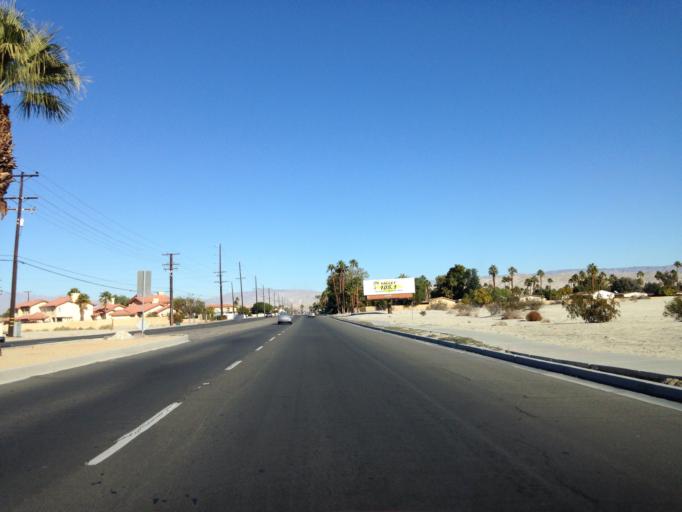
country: US
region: California
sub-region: Riverside County
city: Cathedral City
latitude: 33.8071
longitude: -116.4579
